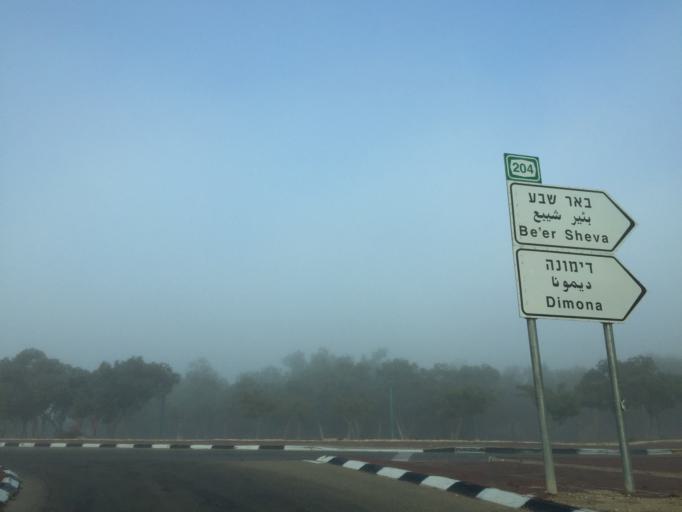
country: IL
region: Southern District
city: Yeroham
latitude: 30.9897
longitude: 34.9116
